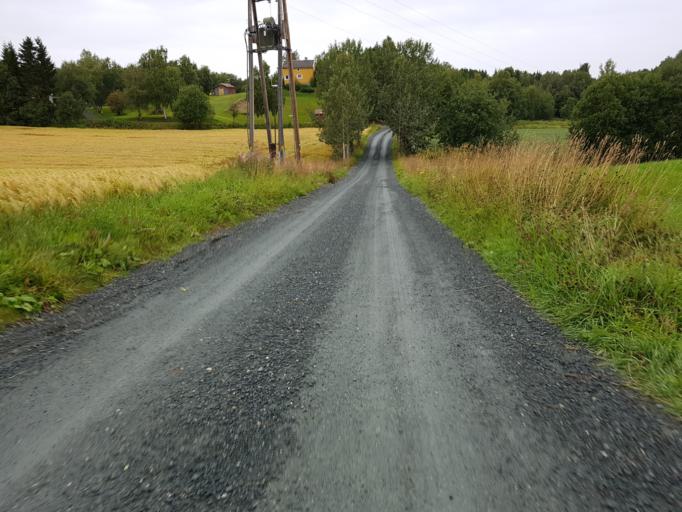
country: NO
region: Sor-Trondelag
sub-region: Trondheim
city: Trondheim
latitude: 63.4005
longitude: 10.4636
